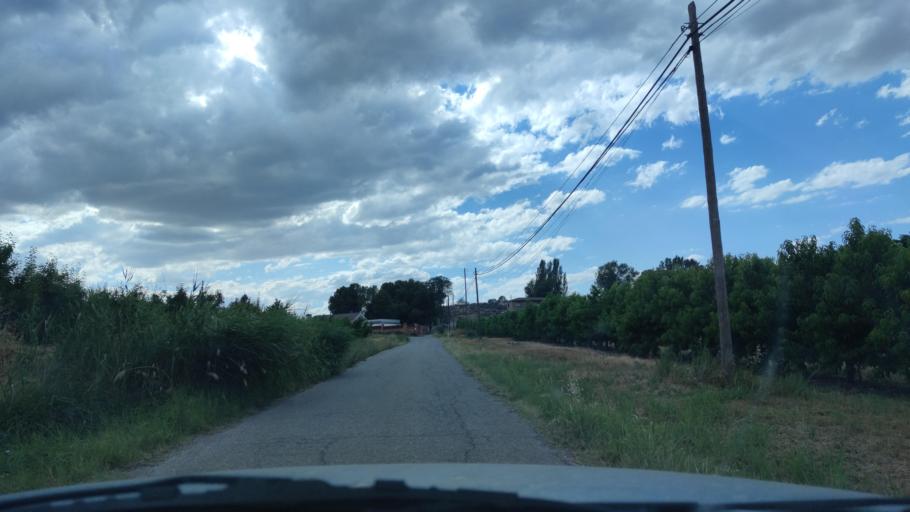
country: ES
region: Catalonia
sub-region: Provincia de Lleida
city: Alpicat
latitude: 41.6285
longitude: 0.5787
